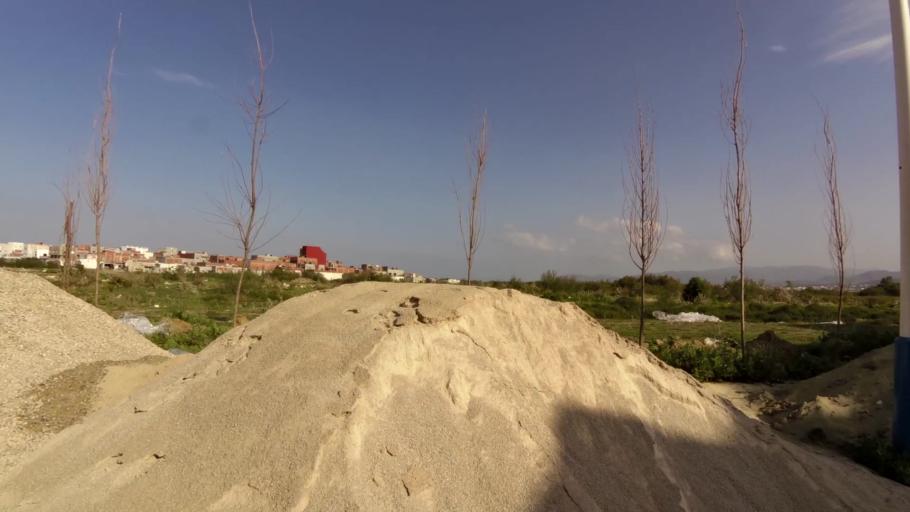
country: MA
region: Tanger-Tetouan
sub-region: Tetouan
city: Martil
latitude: 35.6106
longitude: -5.2810
